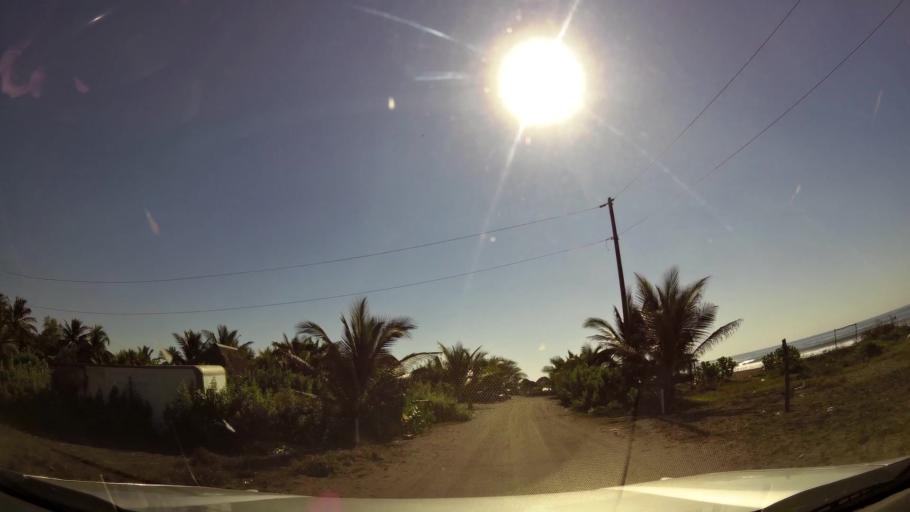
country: GT
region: Jutiapa
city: Pasaco
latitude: 13.8475
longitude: -90.3694
